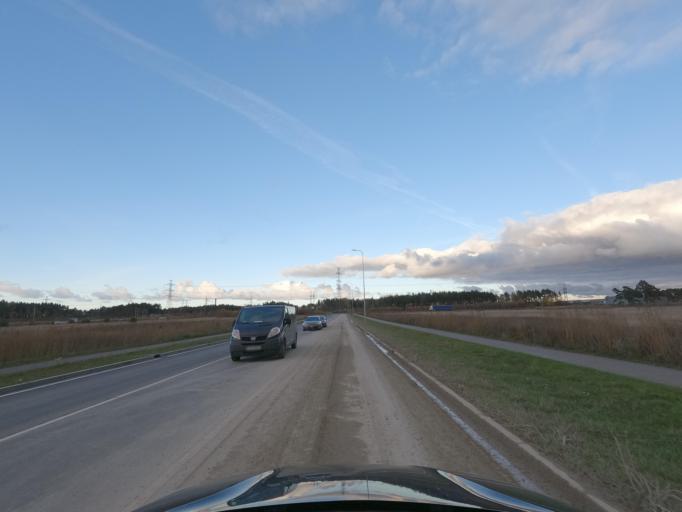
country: EE
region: Harju
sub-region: Saue vald
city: Laagri
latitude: 59.3358
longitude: 24.6013
